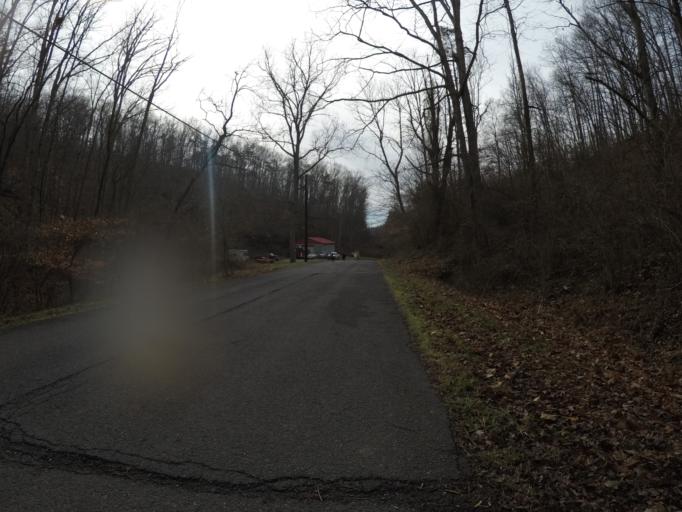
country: US
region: West Virginia
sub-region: Wayne County
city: Lavalette
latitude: 38.3398
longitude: -82.3759
